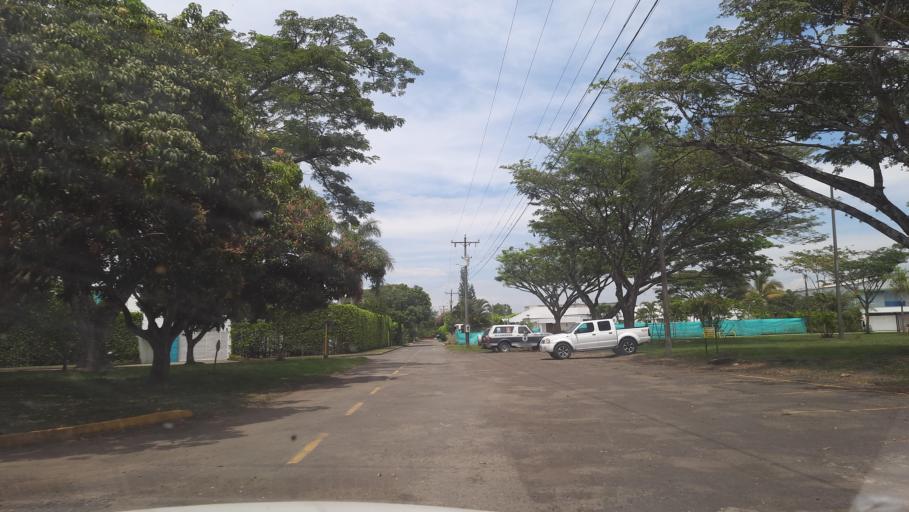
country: CO
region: Valle del Cauca
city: Jamundi
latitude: 3.2685
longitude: -76.5201
